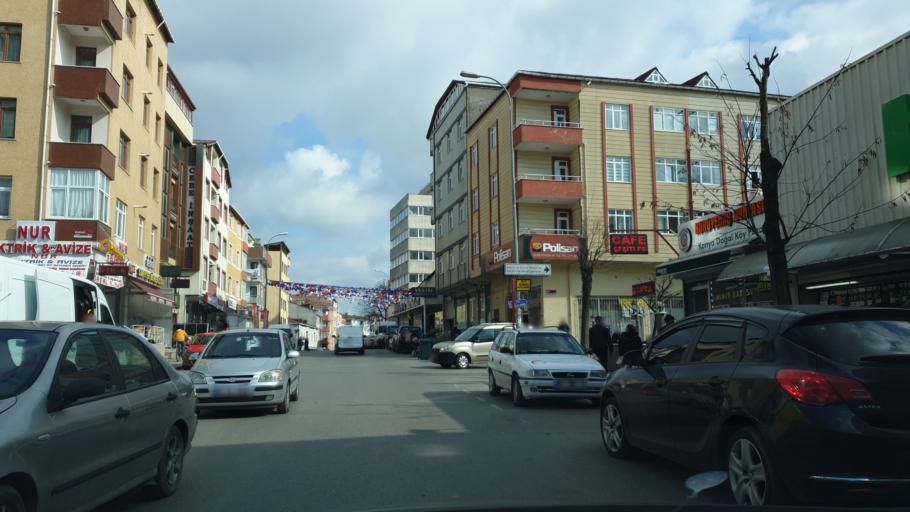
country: TR
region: Istanbul
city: Icmeler
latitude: 40.8677
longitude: 29.2983
